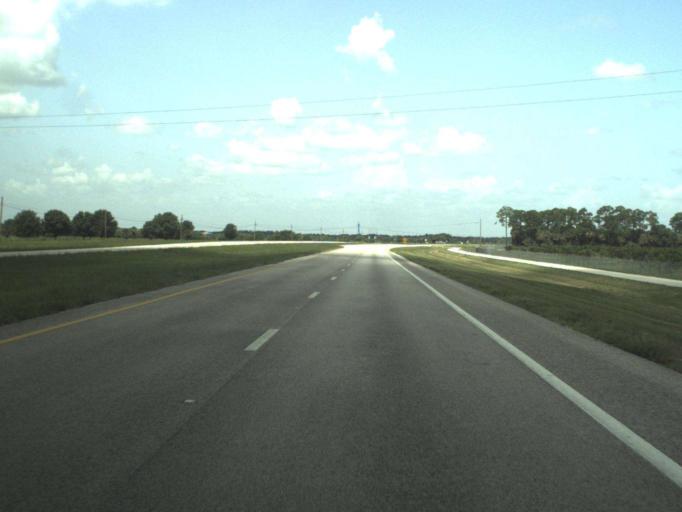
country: US
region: Florida
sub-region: Saint Lucie County
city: Fort Pierce South
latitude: 27.3674
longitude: -80.5256
